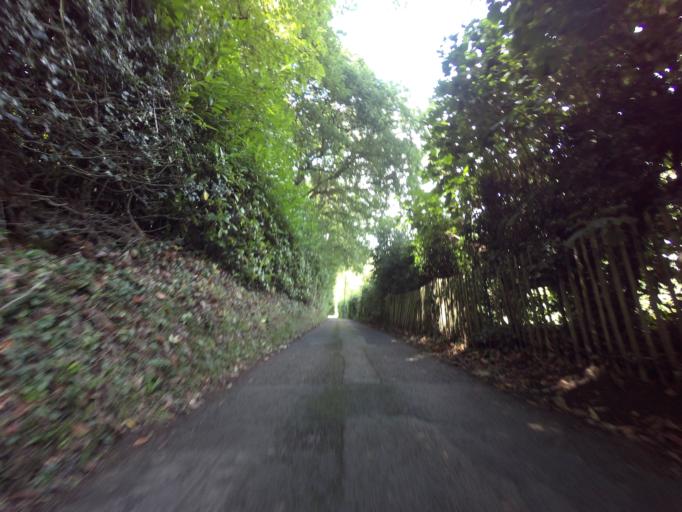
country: GB
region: England
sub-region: Kent
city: Borough Green
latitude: 51.2823
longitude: 0.2742
